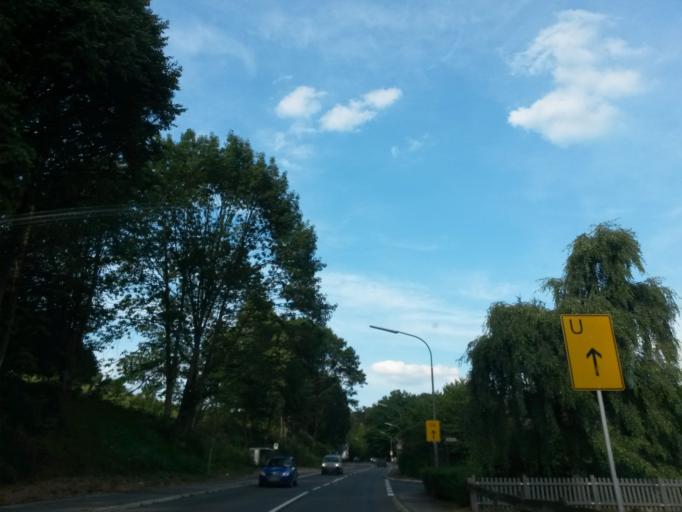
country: DE
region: North Rhine-Westphalia
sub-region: Regierungsbezirk Koln
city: Lindlar
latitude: 51.0252
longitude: 7.3937
